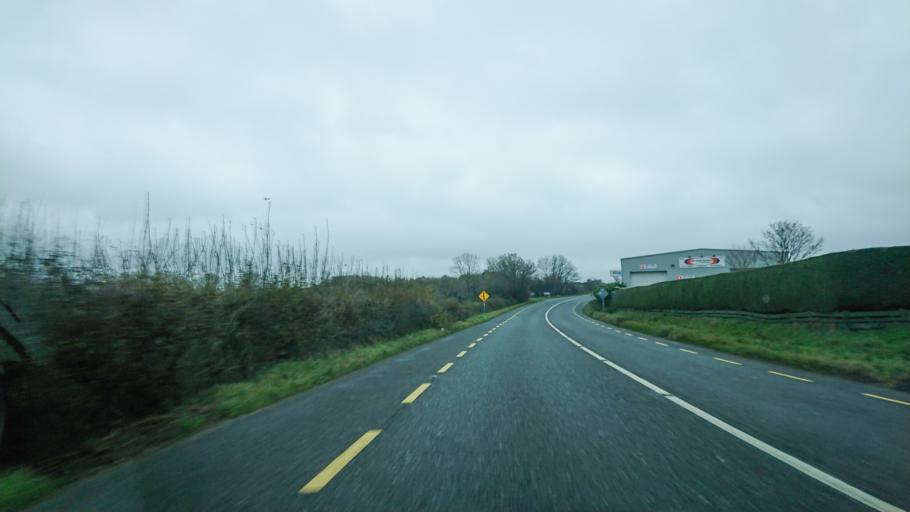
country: IE
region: Leinster
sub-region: Kilkenny
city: Mooncoin
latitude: 52.2904
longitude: -7.2329
